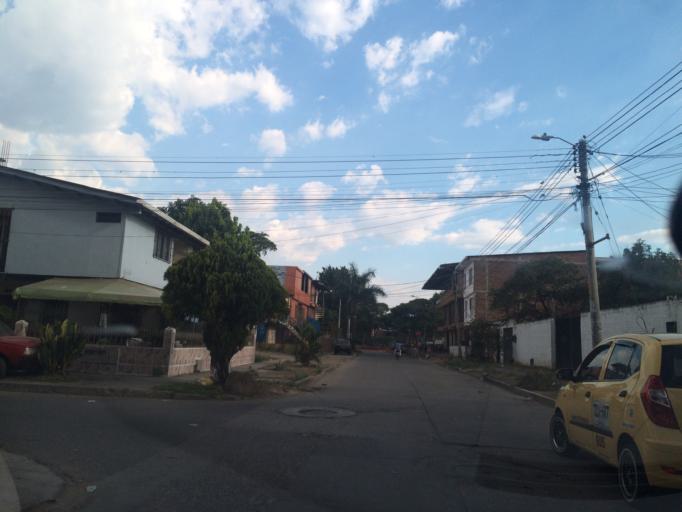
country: CO
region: Valle del Cauca
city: Cali
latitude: 3.3940
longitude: -76.5549
